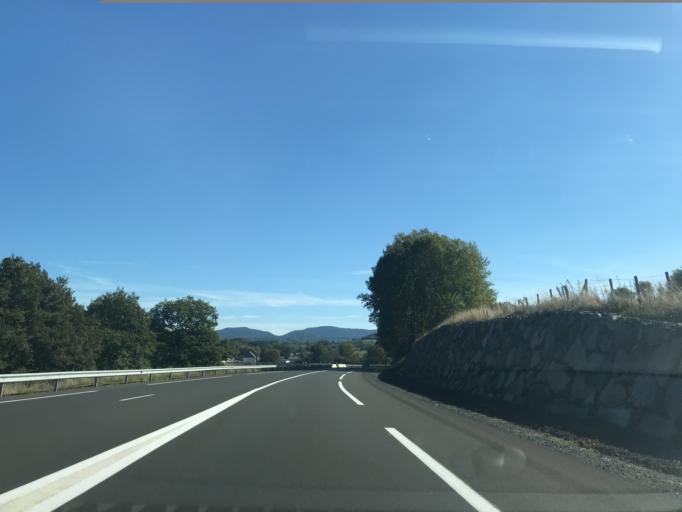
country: FR
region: Auvergne
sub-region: Departement du Puy-de-Dome
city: Gelles
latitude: 45.7315
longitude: 2.8251
